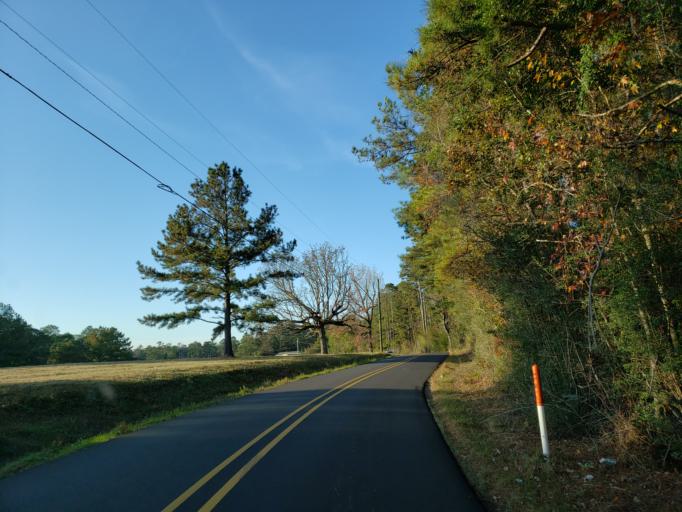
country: US
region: Mississippi
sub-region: Lamar County
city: Arnold Line
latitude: 31.3514
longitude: -89.3581
